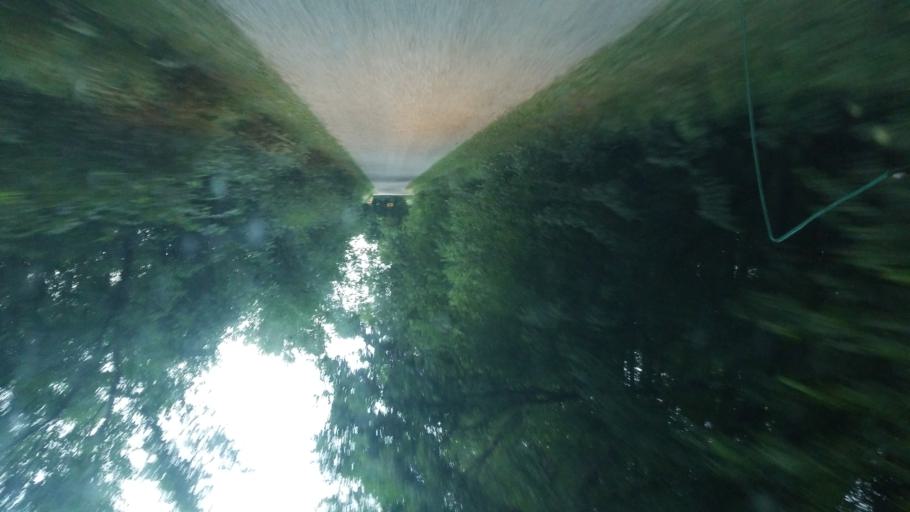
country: US
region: Ohio
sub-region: Defiance County
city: Hicksville
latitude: 41.3668
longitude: -84.8040
